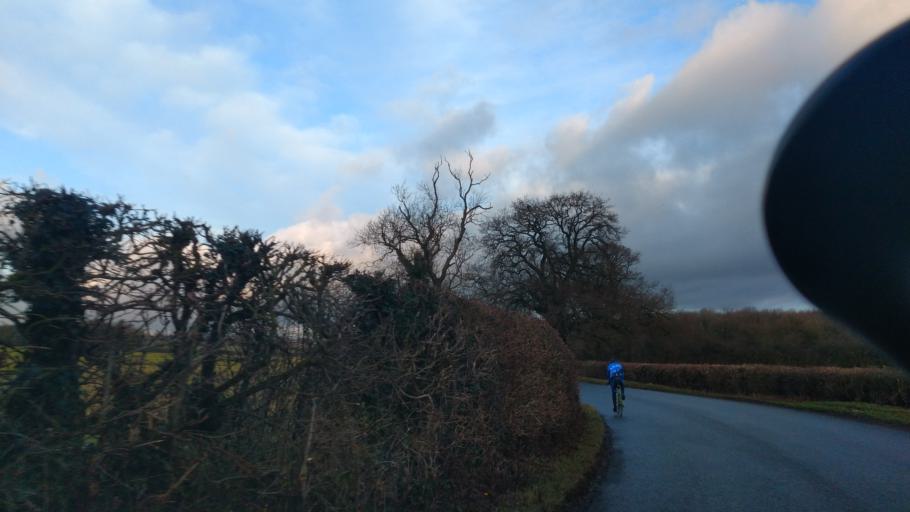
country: GB
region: England
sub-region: Wiltshire
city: Corsham
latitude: 51.4453
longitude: -2.1856
